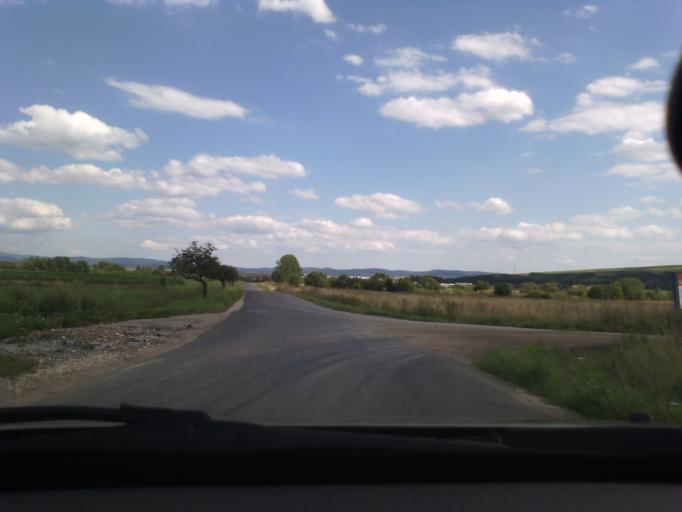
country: SK
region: Presovsky
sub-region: Okres Poprad
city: Nova Lesna
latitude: 49.1227
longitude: 20.3410
